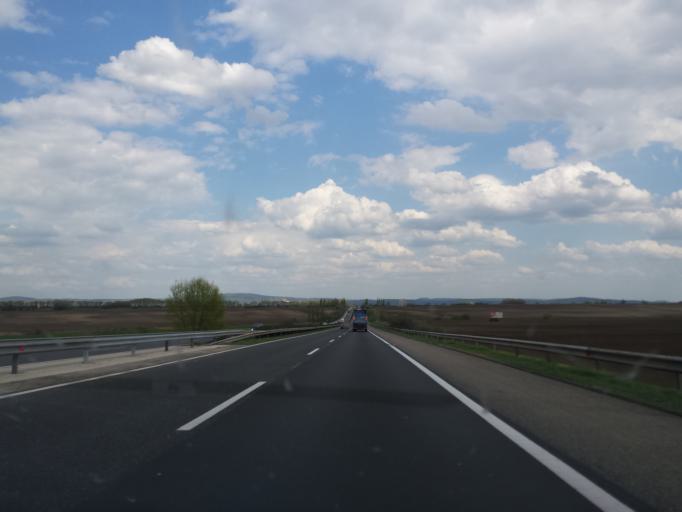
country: HU
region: Pest
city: Zsambek
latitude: 47.5080
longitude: 18.6959
